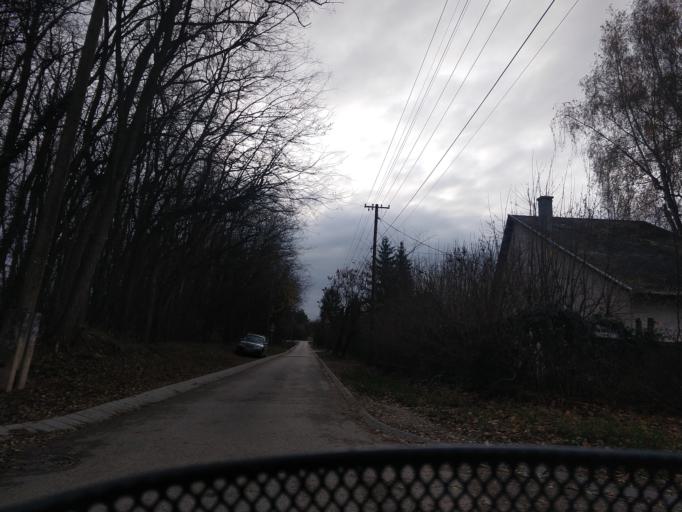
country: HU
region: Pest
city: Veresegyhaz
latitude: 47.6485
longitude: 19.2711
